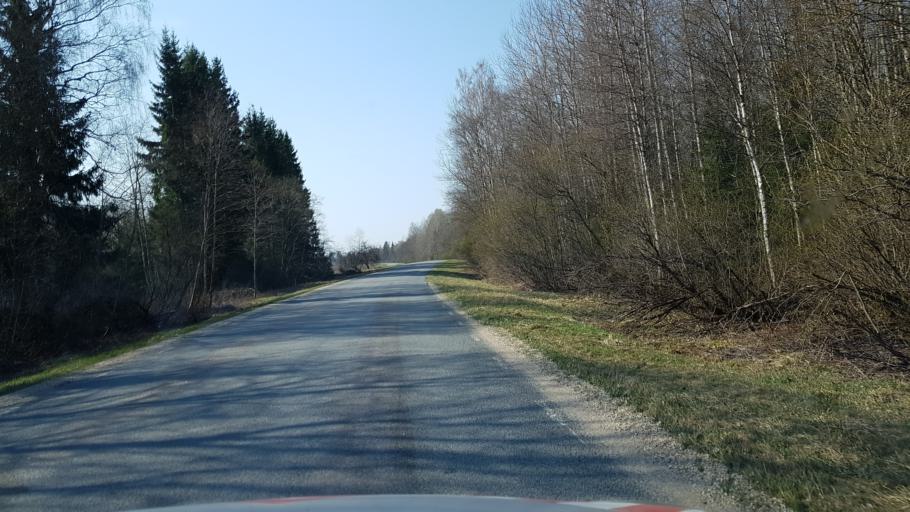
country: EE
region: Raplamaa
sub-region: Maerjamaa vald
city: Marjamaa
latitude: 58.8800
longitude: 24.3836
